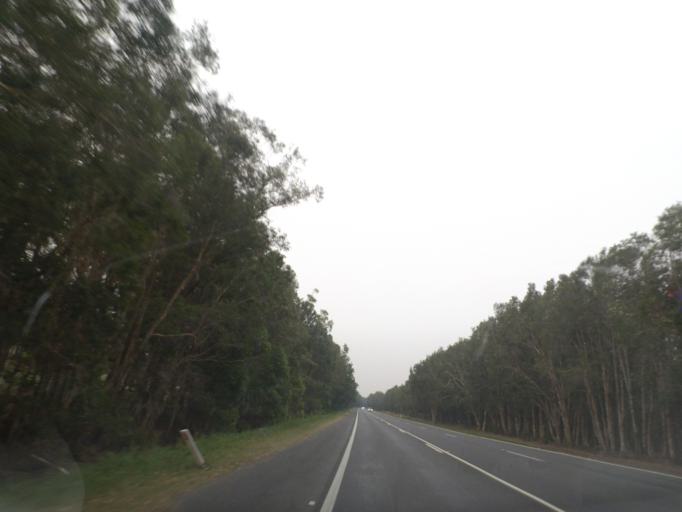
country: AU
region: New South Wales
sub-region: Coffs Harbour
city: Coffs Harbour
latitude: -30.3143
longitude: 153.1144
